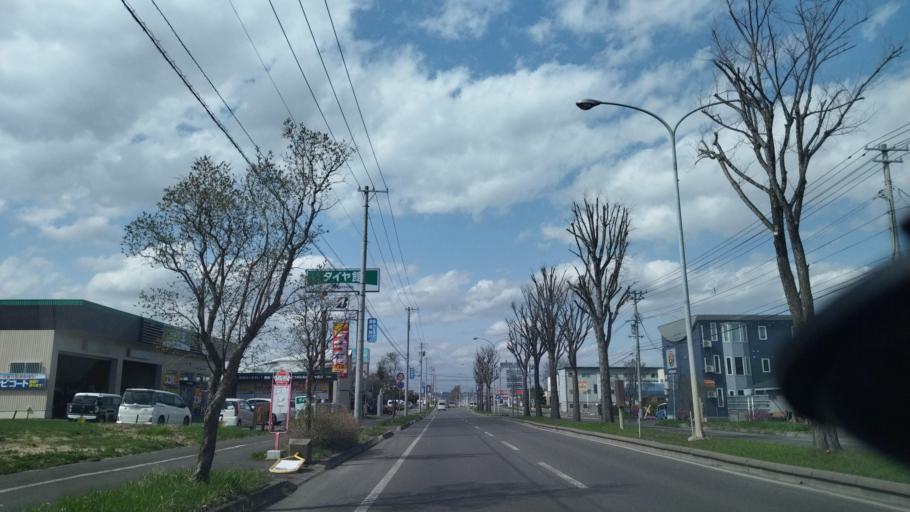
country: JP
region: Hokkaido
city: Obihiro
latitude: 42.9056
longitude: 143.1460
